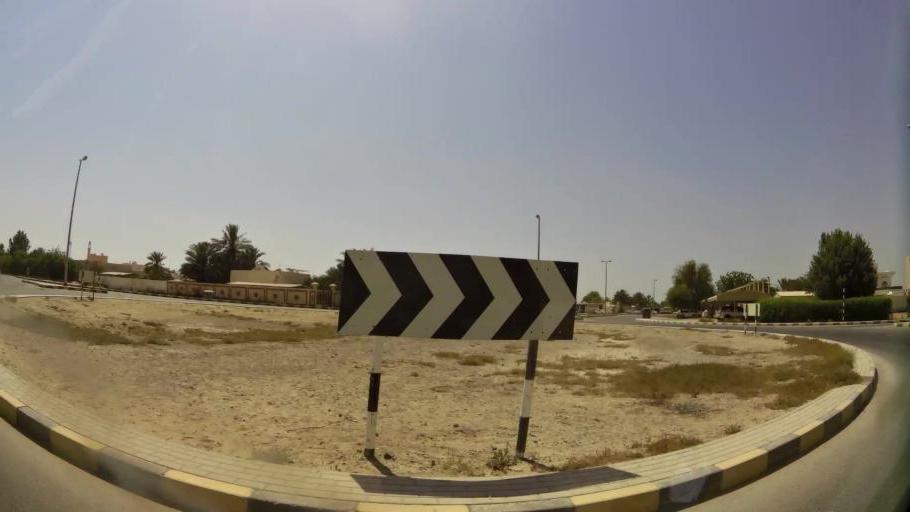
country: AE
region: Ajman
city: Ajman
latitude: 25.4165
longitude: 55.4750
